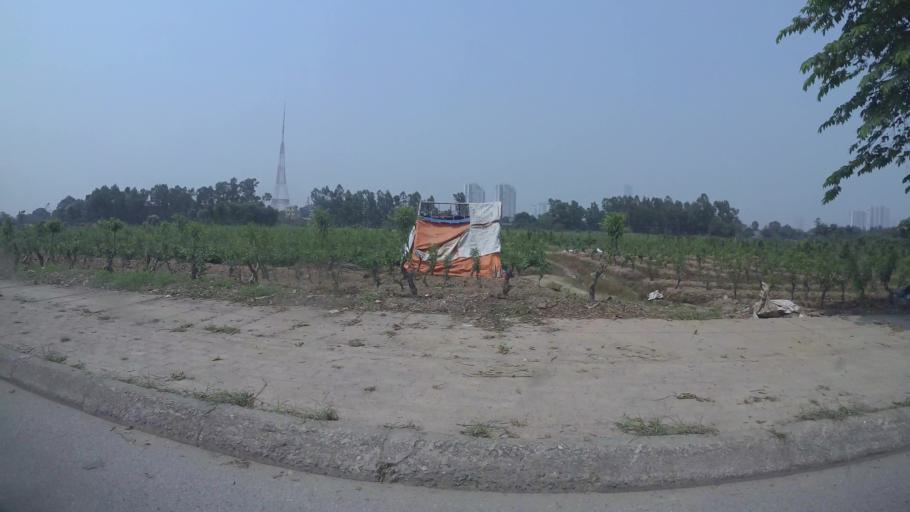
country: VN
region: Ha Noi
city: Ha Dong
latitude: 20.9942
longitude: 105.7651
